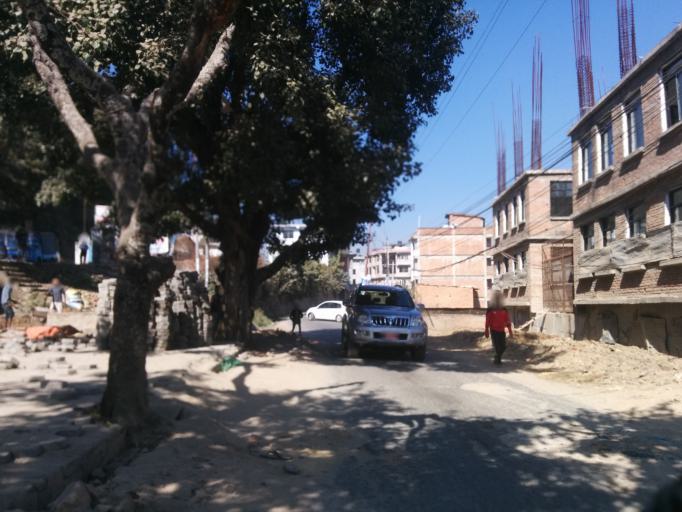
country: NP
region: Central Region
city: Kirtipur
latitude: 27.6776
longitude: 85.2803
